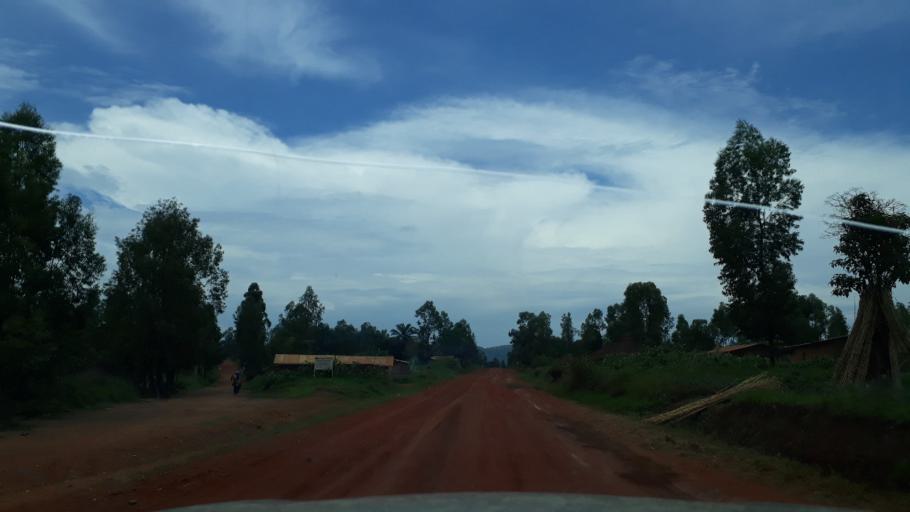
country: CD
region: Eastern Province
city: Bunia
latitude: 1.6809
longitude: 30.2777
